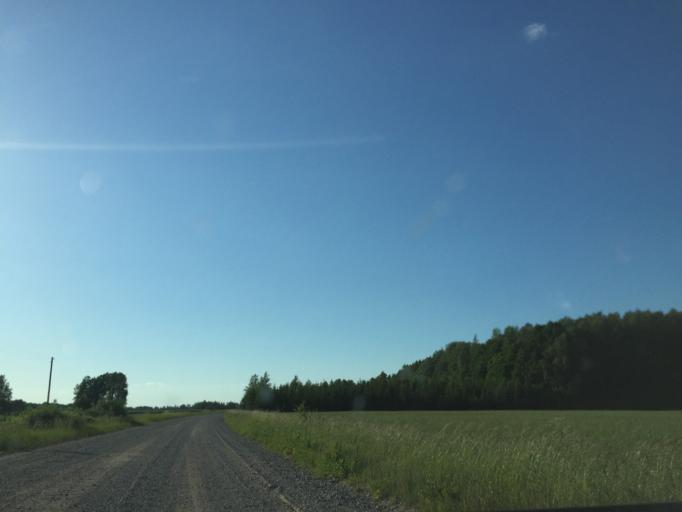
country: LV
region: Kandava
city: Kandava
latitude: 56.8385
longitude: 22.7158
